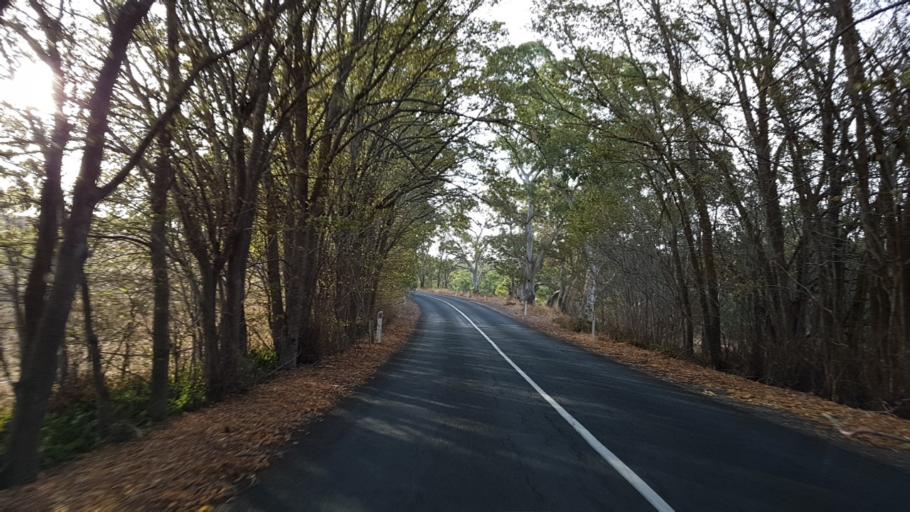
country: AU
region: South Australia
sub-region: Adelaide Hills
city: Woodside
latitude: -34.9801
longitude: 138.8934
